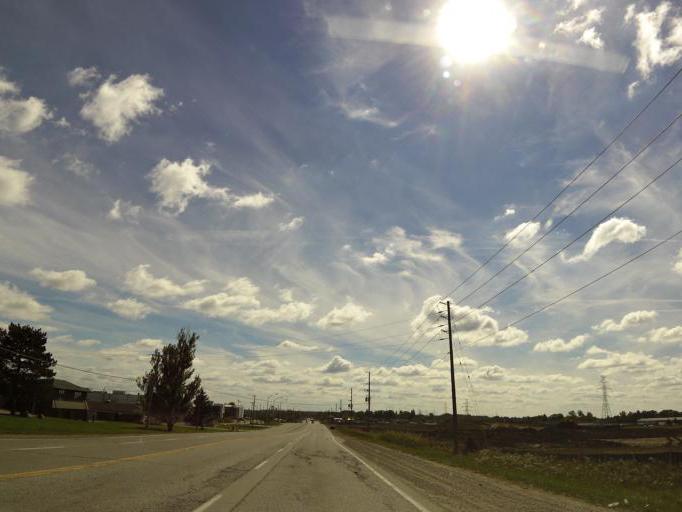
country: CA
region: Ontario
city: London
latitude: 42.9288
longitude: -81.2792
